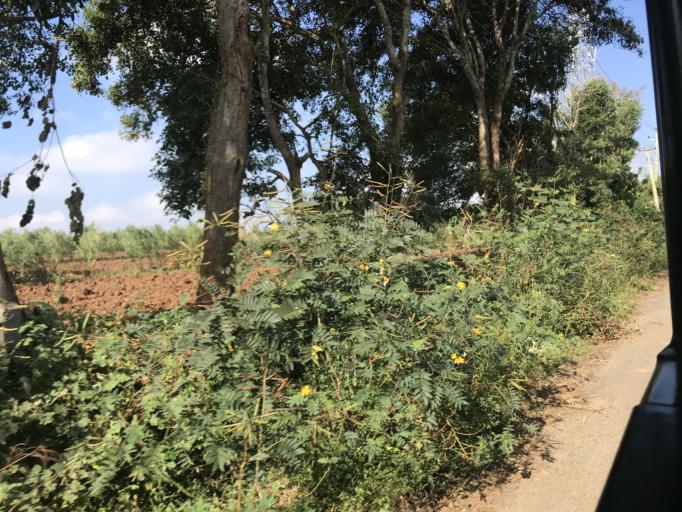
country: IN
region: Karnataka
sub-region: Mysore
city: Sargur
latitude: 11.9436
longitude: 76.2673
